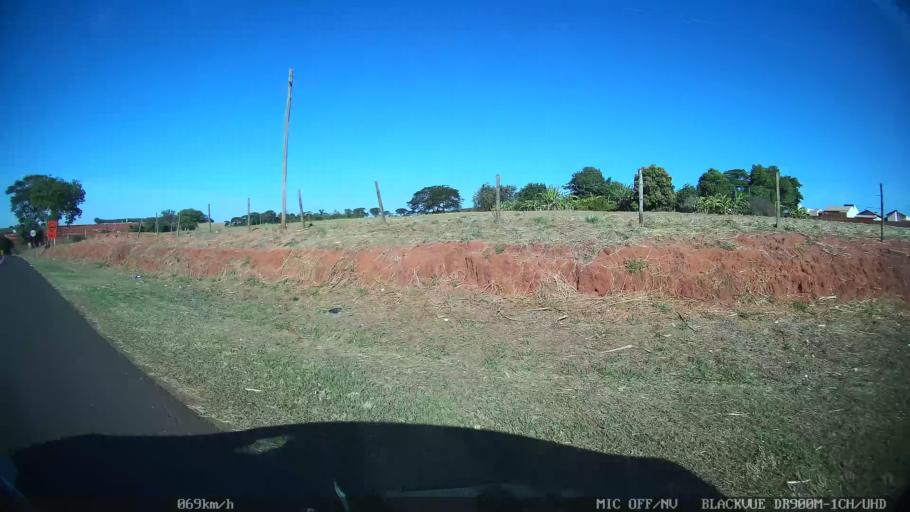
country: BR
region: Sao Paulo
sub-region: Olimpia
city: Olimpia
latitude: -20.7374
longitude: -48.8809
